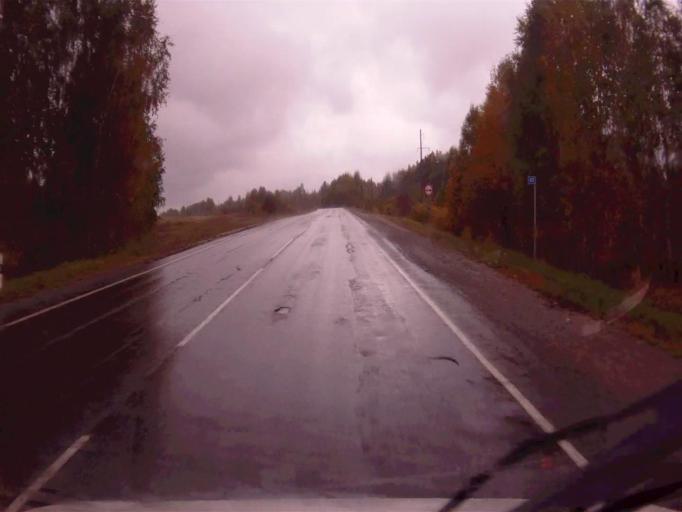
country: RU
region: Chelyabinsk
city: Argayash
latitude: 55.4849
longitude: 60.7412
